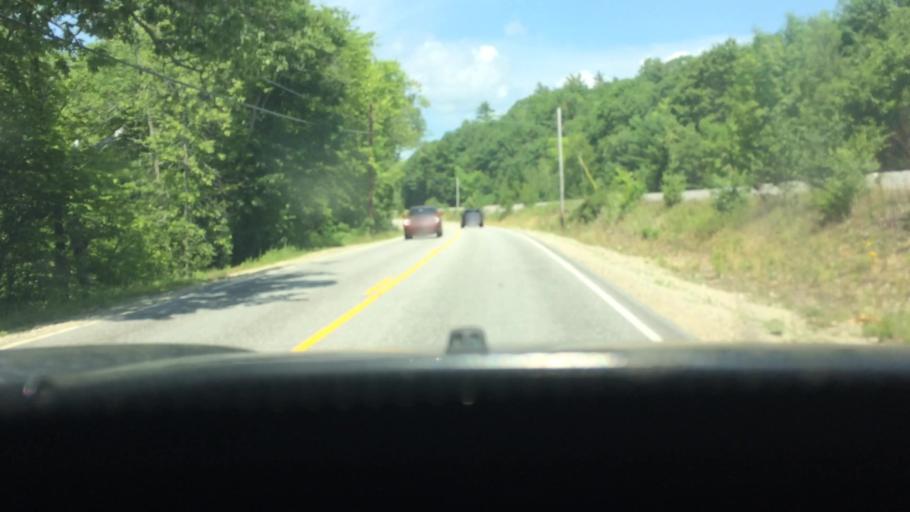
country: US
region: Maine
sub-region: Androscoggin County
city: Mechanic Falls
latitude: 44.1242
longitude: -70.4327
